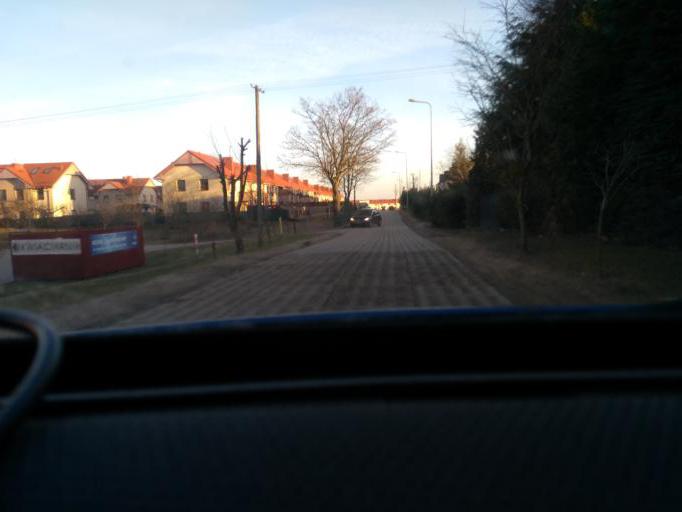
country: PL
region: Pomeranian Voivodeship
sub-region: Powiat kartuski
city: Banino
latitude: 54.3880
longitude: 18.3829
